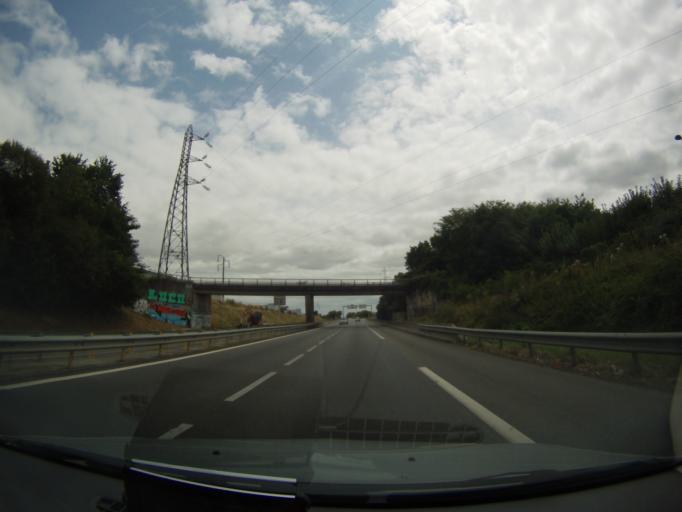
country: FR
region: Pays de la Loire
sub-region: Departement de la Loire-Atlantique
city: Sainte-Luce-sur-Loire
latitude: 47.2499
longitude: -1.5083
